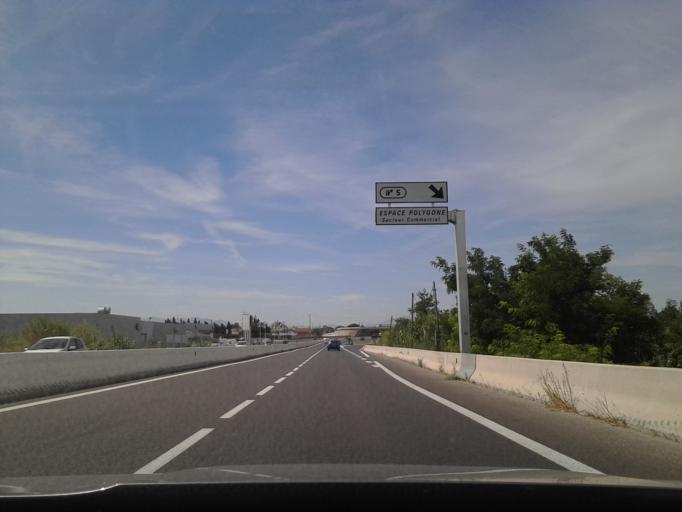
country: FR
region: Languedoc-Roussillon
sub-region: Departement des Pyrenees-Orientales
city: Pia
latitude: 42.7484
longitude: 2.8942
